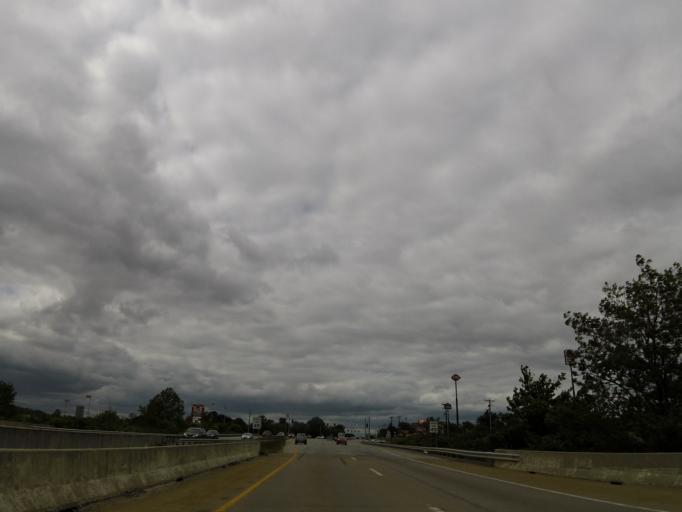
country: US
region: Kentucky
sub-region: Scott County
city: Georgetown
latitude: 38.2110
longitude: -84.5393
